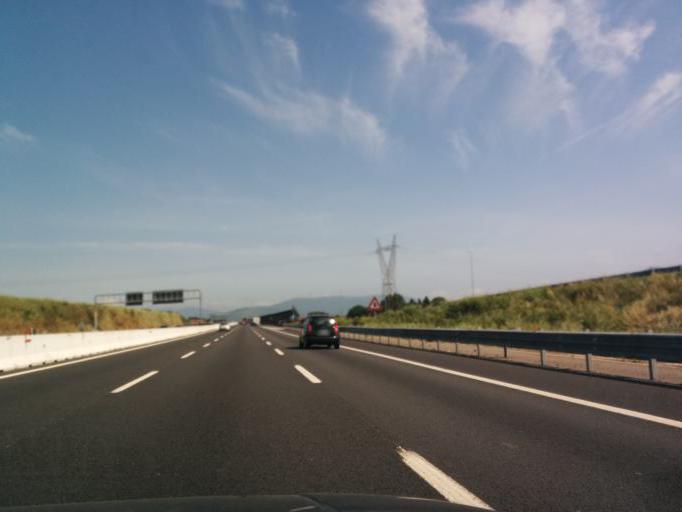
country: IT
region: Tuscany
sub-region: Province of Florence
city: Mantignano-Ugnano
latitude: 43.7782
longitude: 11.1613
